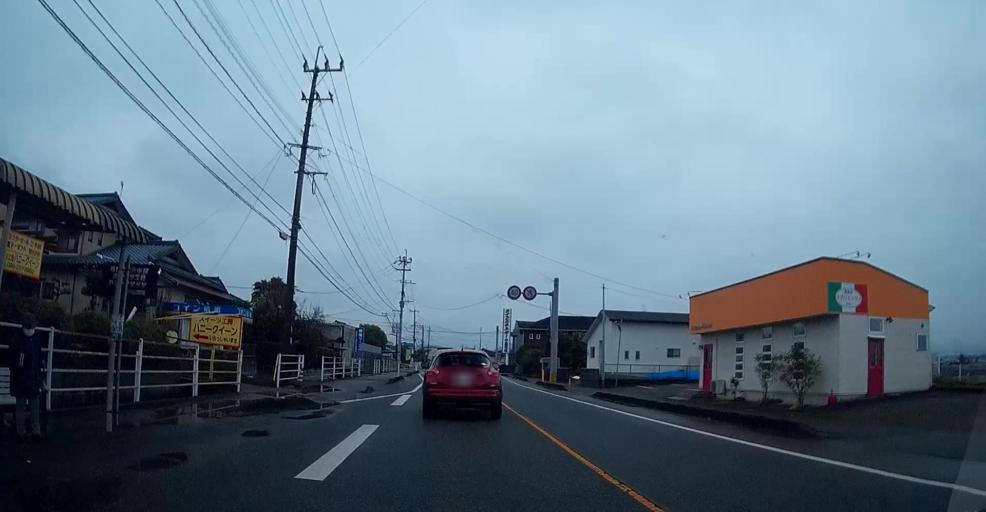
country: JP
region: Kumamoto
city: Kumamoto
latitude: 32.7465
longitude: 130.7386
